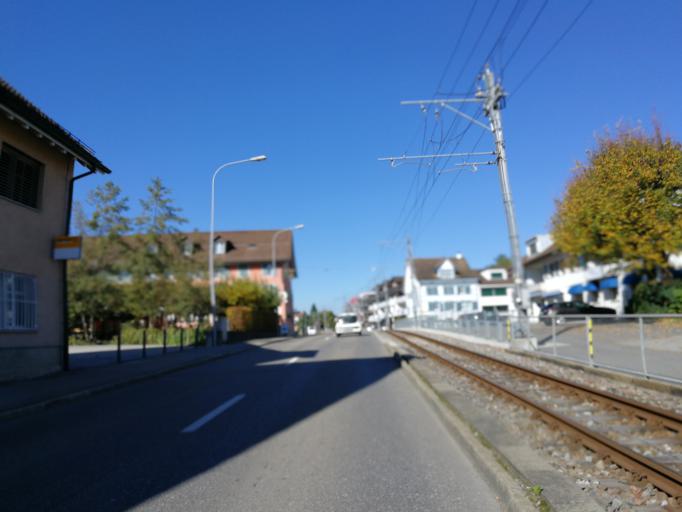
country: CH
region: Zurich
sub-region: Bezirk Uster
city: Egg
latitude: 47.3003
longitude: 8.6902
